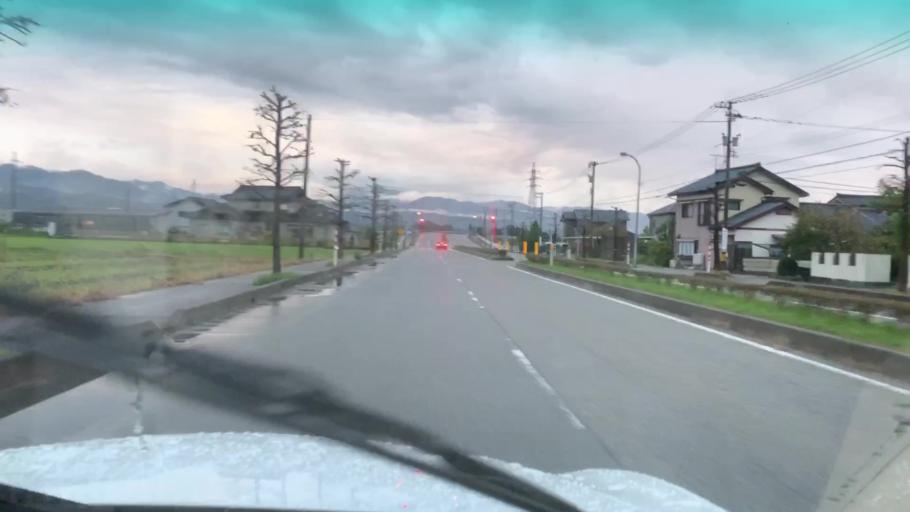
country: JP
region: Toyama
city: Kamiichi
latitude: 36.6975
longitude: 137.3427
